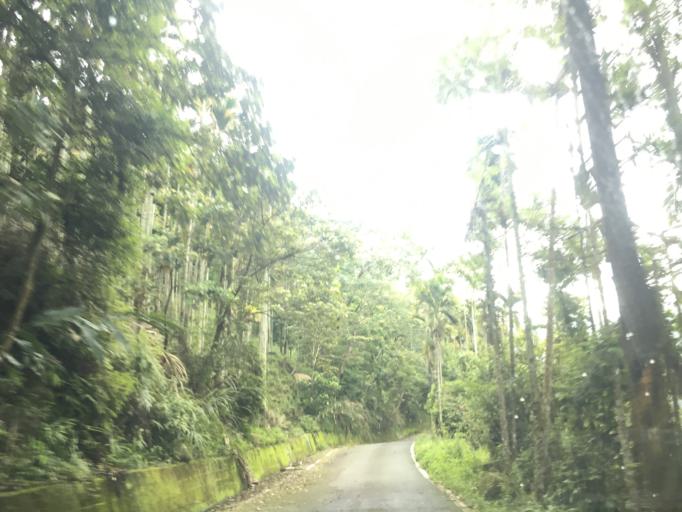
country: TW
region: Taiwan
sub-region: Yunlin
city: Douliu
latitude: 23.5694
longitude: 120.6341
